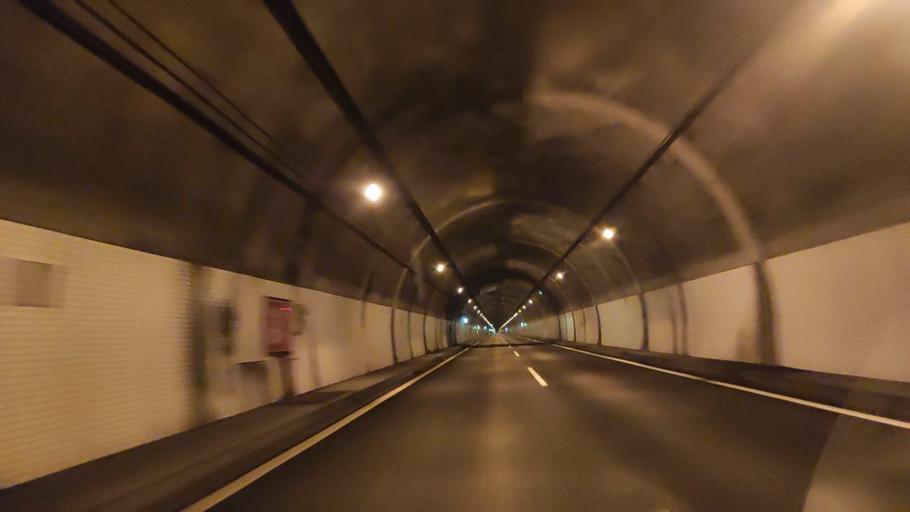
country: JP
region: Niigata
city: Itoigawa
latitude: 37.0099
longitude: 137.7566
